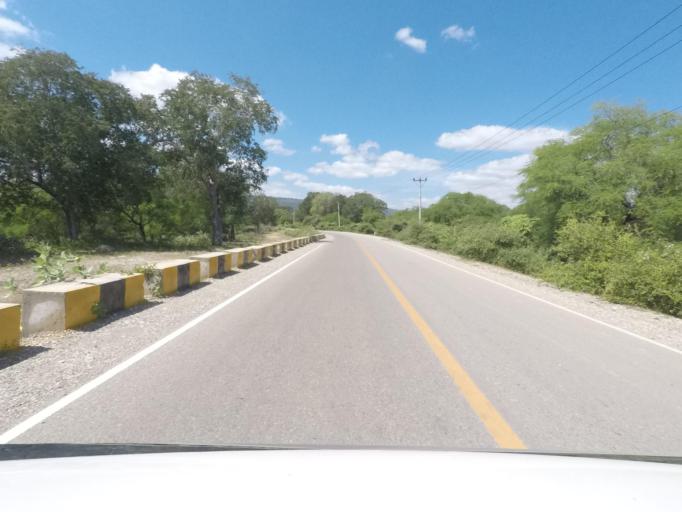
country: TL
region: Lautem
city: Lospalos
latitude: -8.3744
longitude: 126.8876
